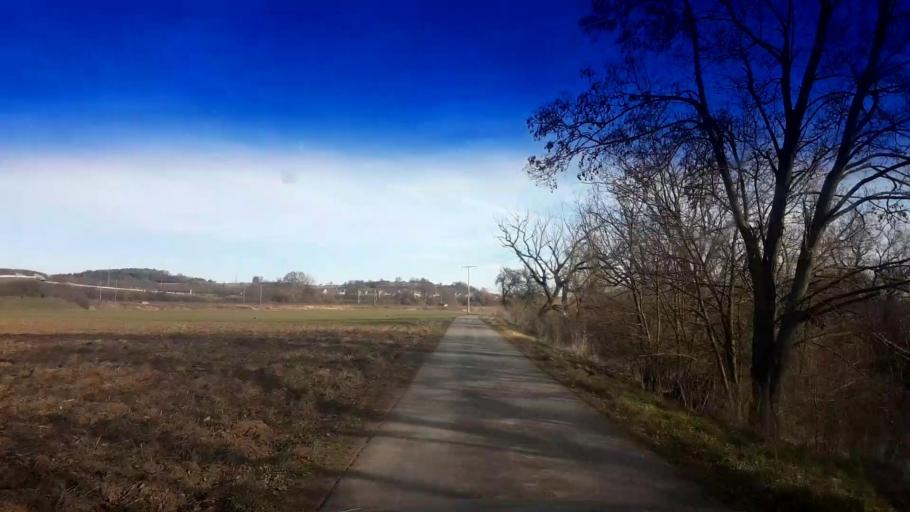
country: DE
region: Bavaria
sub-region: Regierungsbezirk Unterfranken
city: Stettfeld
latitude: 49.9503
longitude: 10.7386
